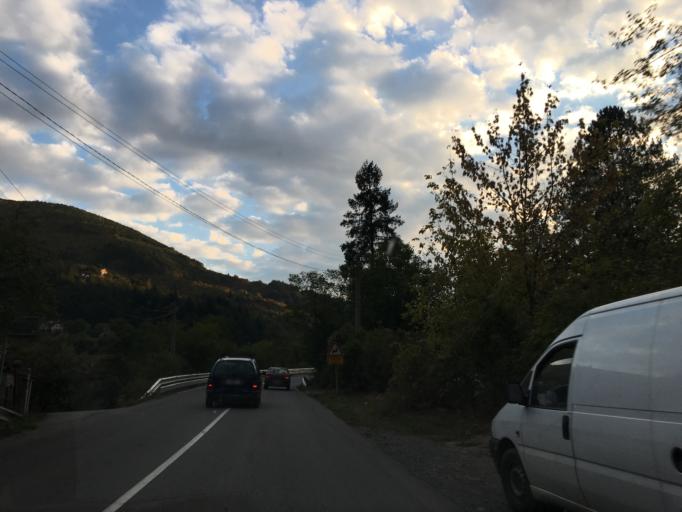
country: BG
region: Sofiya
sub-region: Obshtina Svoge
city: Svoge
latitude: 42.8816
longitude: 23.3913
